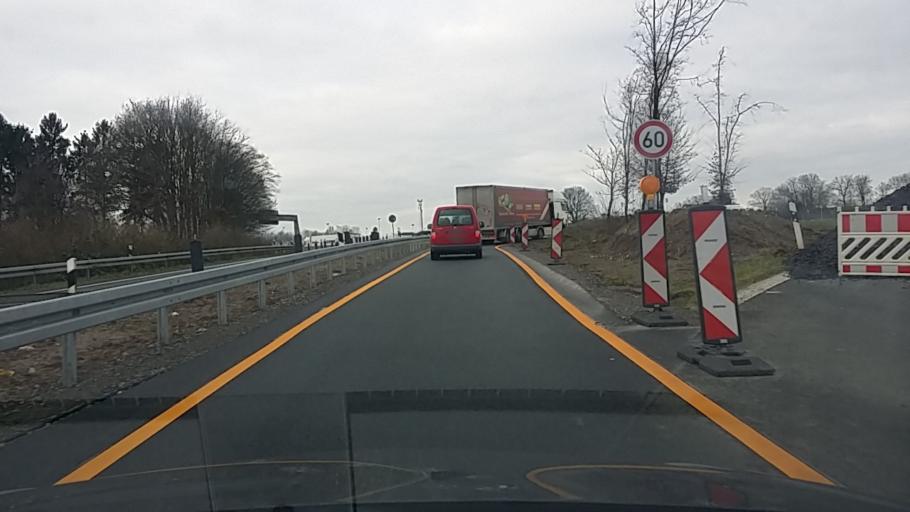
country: DE
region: North Rhine-Westphalia
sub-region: Regierungsbezirk Munster
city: Lotte
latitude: 52.2674
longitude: 7.9244
